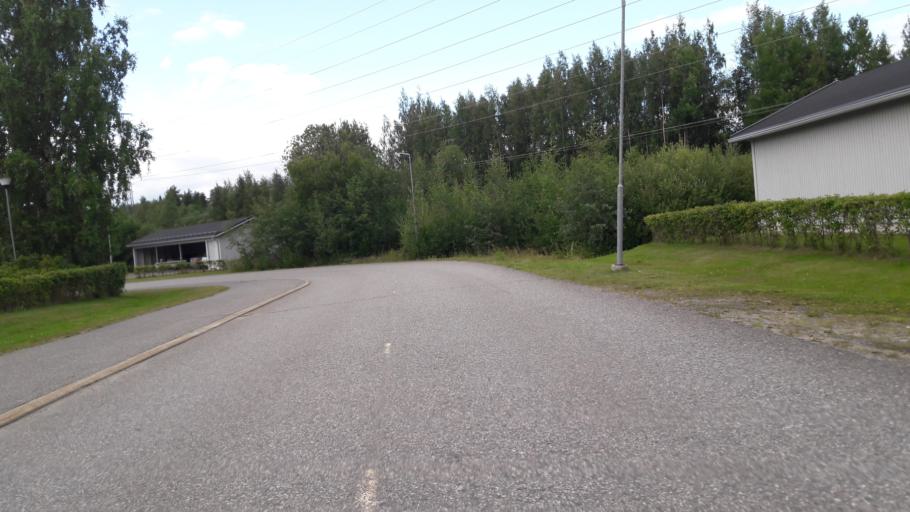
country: FI
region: North Karelia
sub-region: Joensuu
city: Joensuu
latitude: 62.5918
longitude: 29.8040
